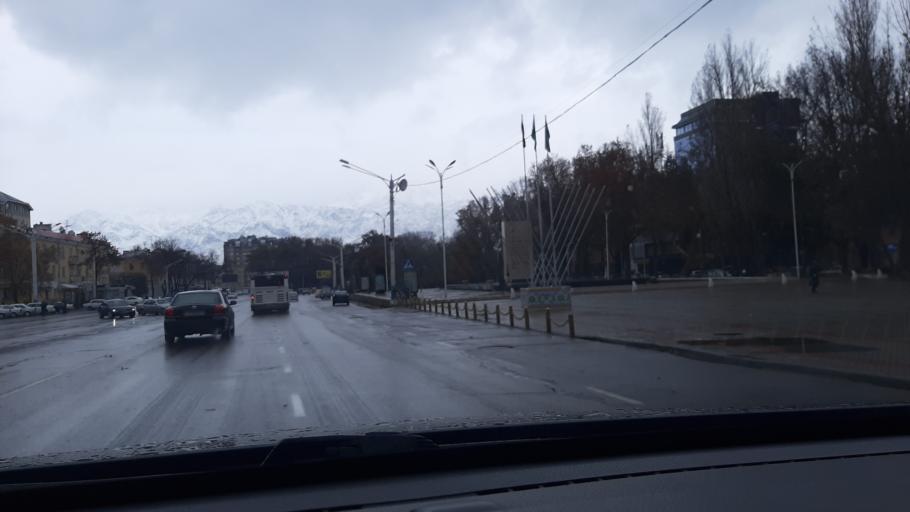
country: TJ
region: Viloyati Sughd
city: Khujand
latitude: 40.2832
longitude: 69.6238
